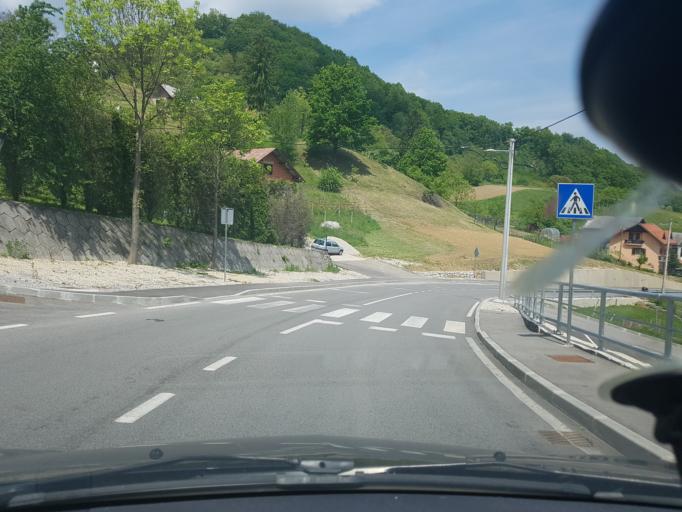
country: SI
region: Rogatec
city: Rogatec
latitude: 46.2155
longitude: 15.6895
